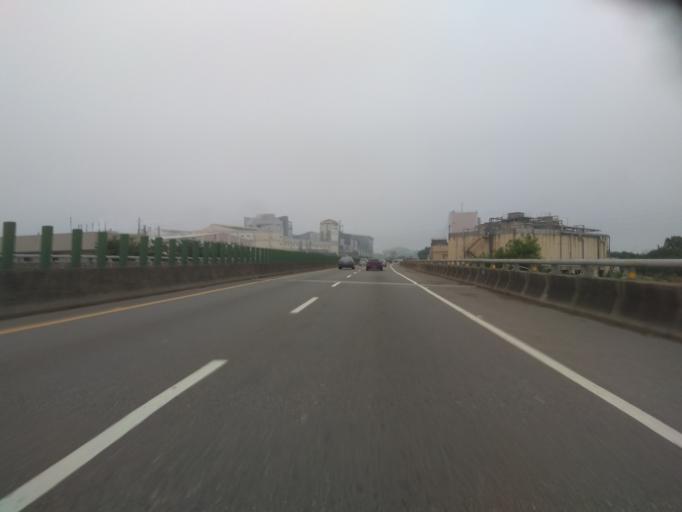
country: TW
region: Taiwan
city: Taoyuan City
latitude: 24.9542
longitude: 121.1551
